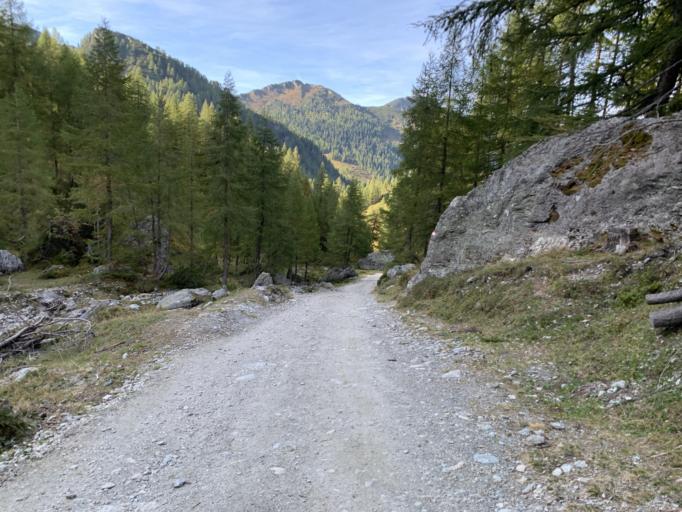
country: AT
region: Salzburg
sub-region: Politischer Bezirk Tamsweg
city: Tweng
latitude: 47.2941
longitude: 13.6290
